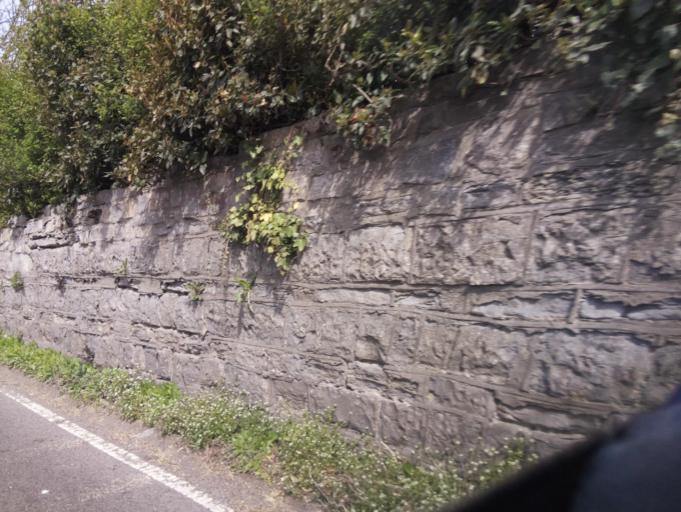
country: GB
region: England
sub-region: Somerset
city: Street
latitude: 51.1294
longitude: -2.8120
